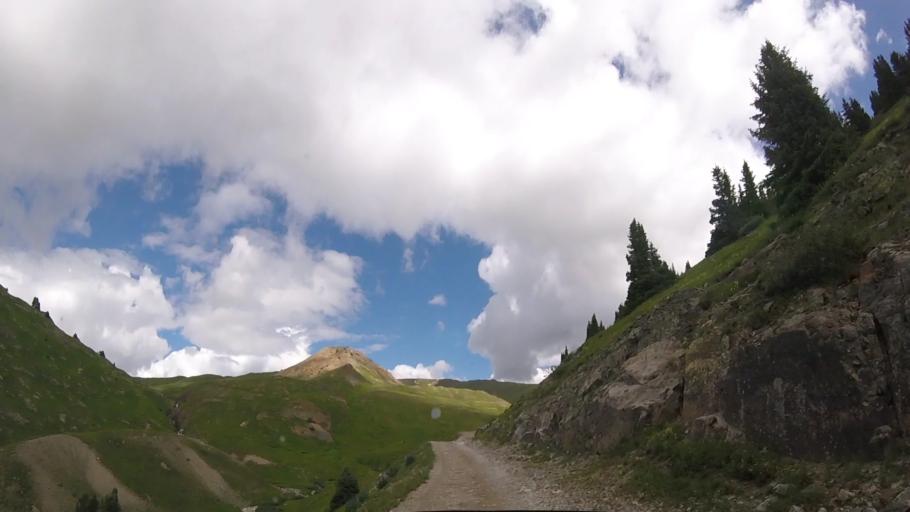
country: US
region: Colorado
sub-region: Ouray County
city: Ouray
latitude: 37.9441
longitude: -107.5740
